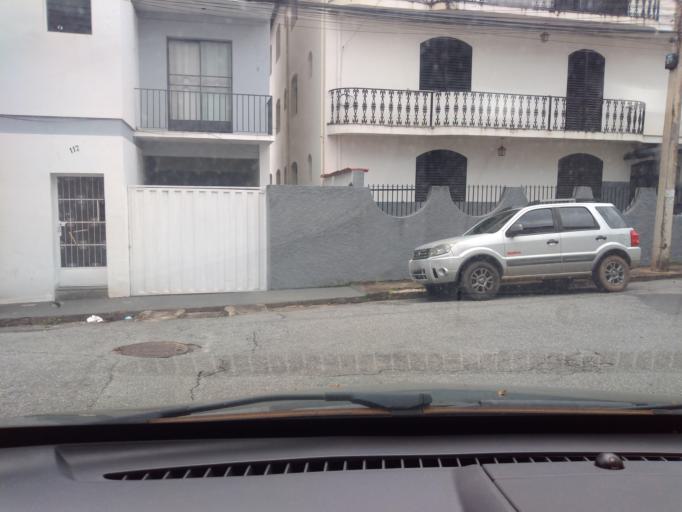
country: BR
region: Minas Gerais
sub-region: Lavras
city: Lavras
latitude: -21.2372
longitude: -44.9969
